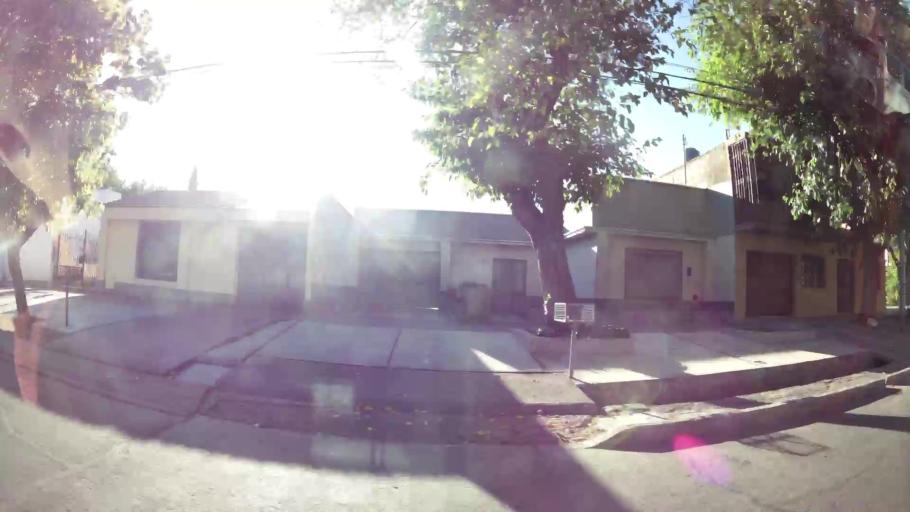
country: AR
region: Mendoza
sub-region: Departamento de Godoy Cruz
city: Godoy Cruz
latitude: -32.9389
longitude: -68.8473
